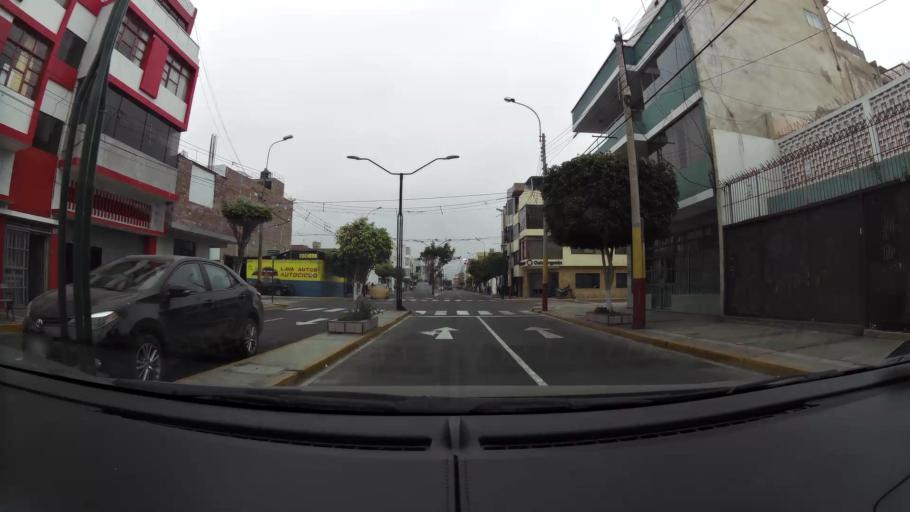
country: PE
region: Ancash
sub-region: Provincia de Santa
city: Chimbote
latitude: -9.0756
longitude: -78.5970
